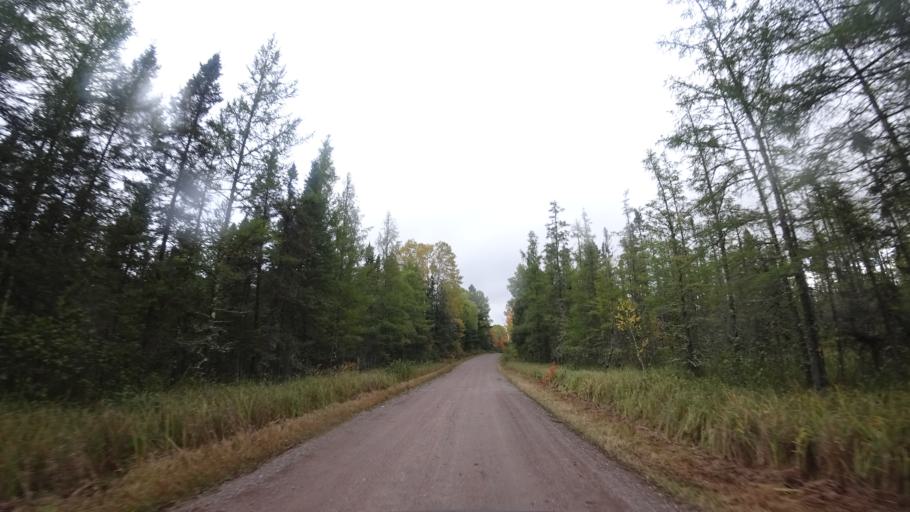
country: US
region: Wisconsin
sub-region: Sawyer County
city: Little Round Lake
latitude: 46.0697
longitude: -90.9942
